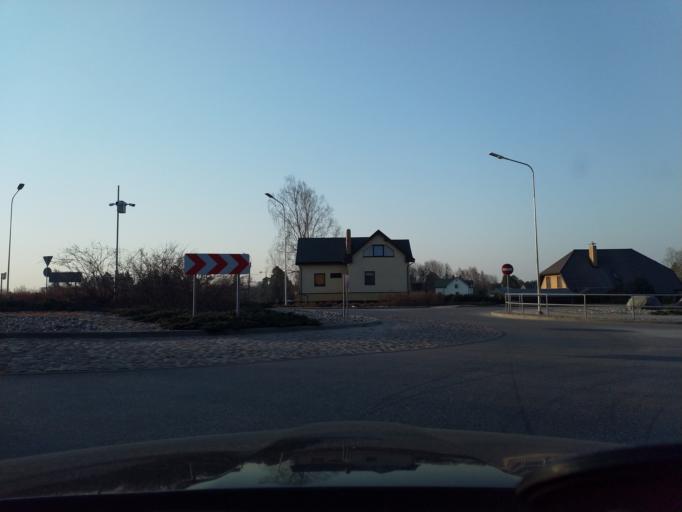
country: LV
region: Grobina
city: Grobina
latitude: 56.5349
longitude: 21.1891
